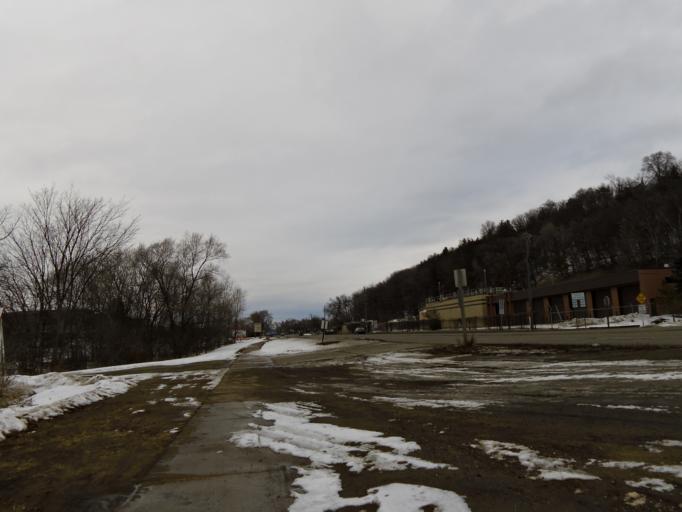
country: US
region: Wisconsin
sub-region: Saint Croix County
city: Hudson
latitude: 44.9655
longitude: -92.7548
